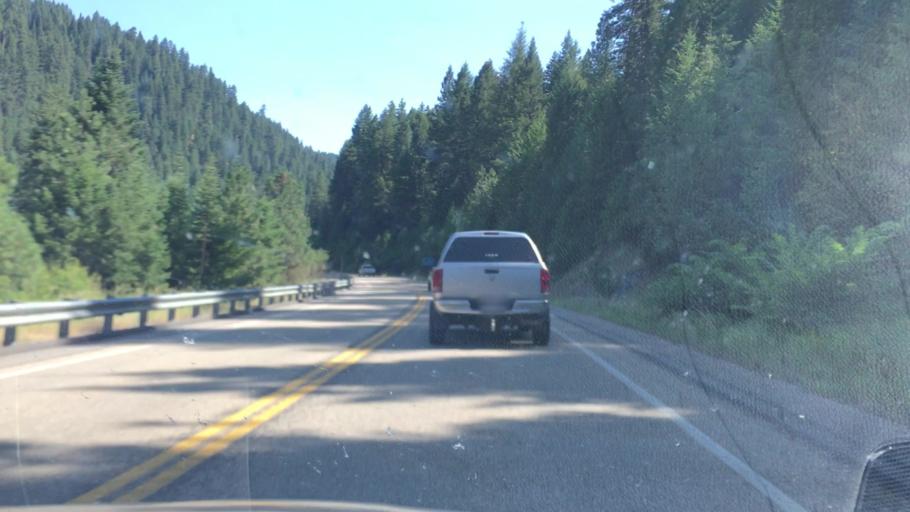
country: US
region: Idaho
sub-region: Valley County
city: Cascade
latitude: 44.1675
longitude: -116.1208
